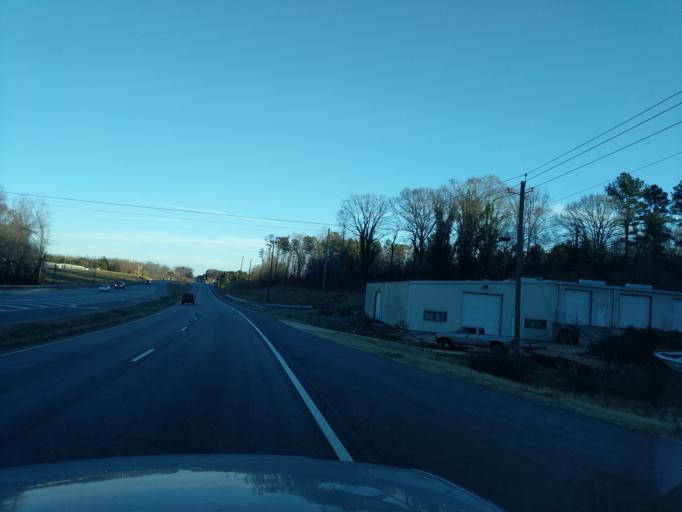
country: US
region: Georgia
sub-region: Stephens County
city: Toccoa
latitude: 34.5241
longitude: -83.2474
